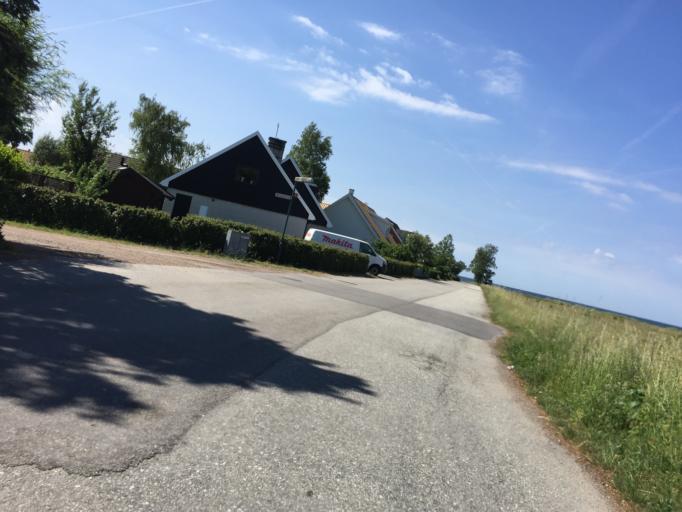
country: SE
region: Skane
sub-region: Trelleborgs Kommun
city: Trelleborg
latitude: 55.3583
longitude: 13.2300
